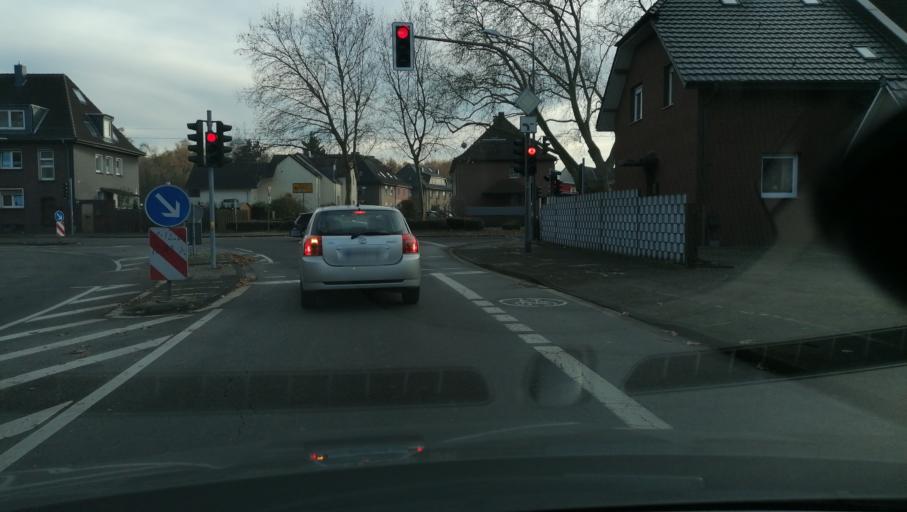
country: DE
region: North Rhine-Westphalia
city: Castrop-Rauxel
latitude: 51.5868
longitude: 7.3218
